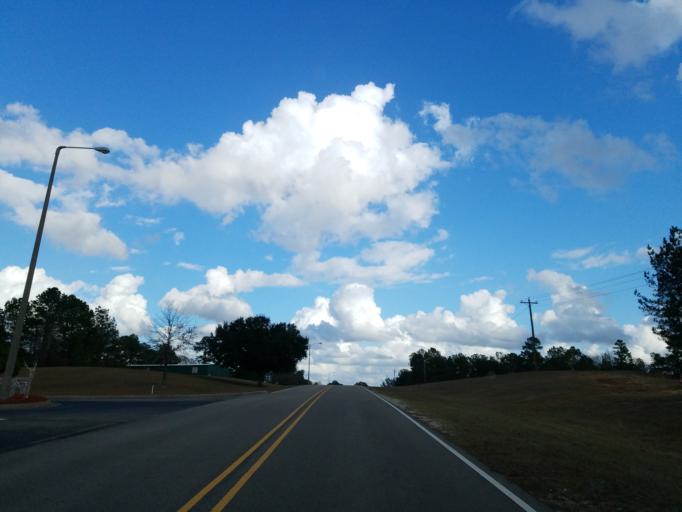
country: US
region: Mississippi
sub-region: Forrest County
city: Rawls Springs
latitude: 31.4693
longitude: -89.3307
